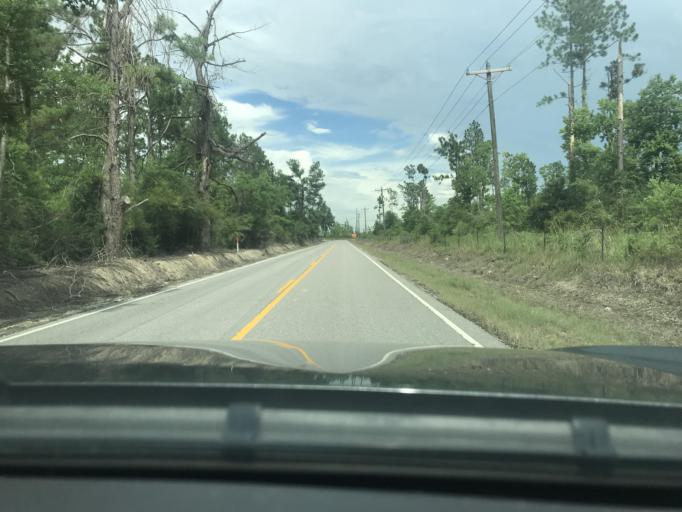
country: US
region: Louisiana
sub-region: Calcasieu Parish
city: Moss Bluff
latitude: 30.3885
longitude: -93.2357
